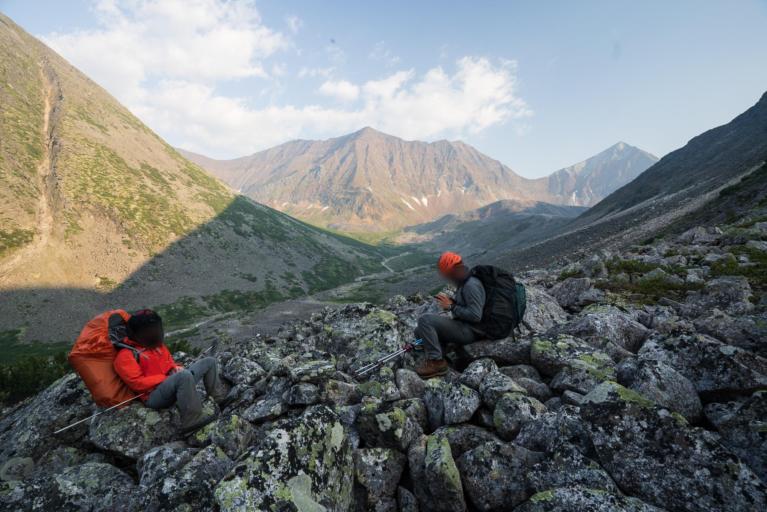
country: RU
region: Transbaikal Territory
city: Kuanda
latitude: 56.7946
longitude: 116.8305
